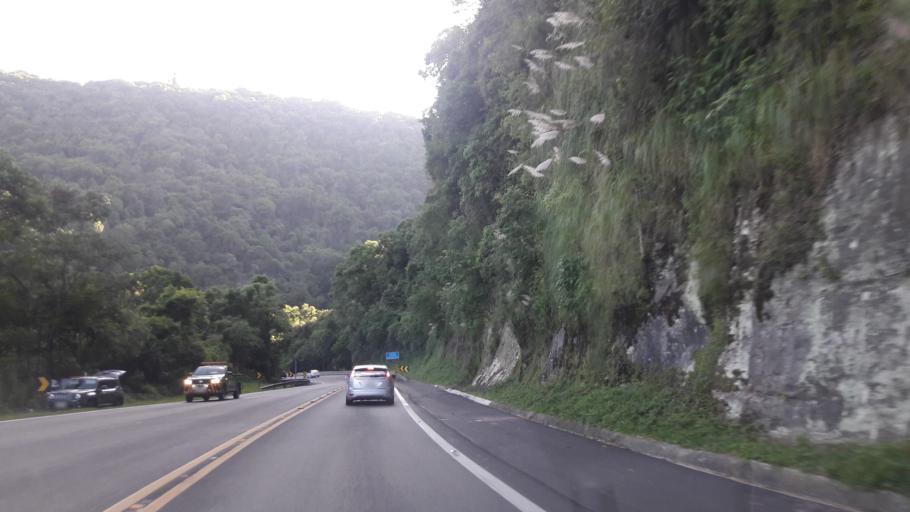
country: BR
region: Parana
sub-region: Prudentopolis
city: Prudentopolis
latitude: -25.3206
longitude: -51.1955
